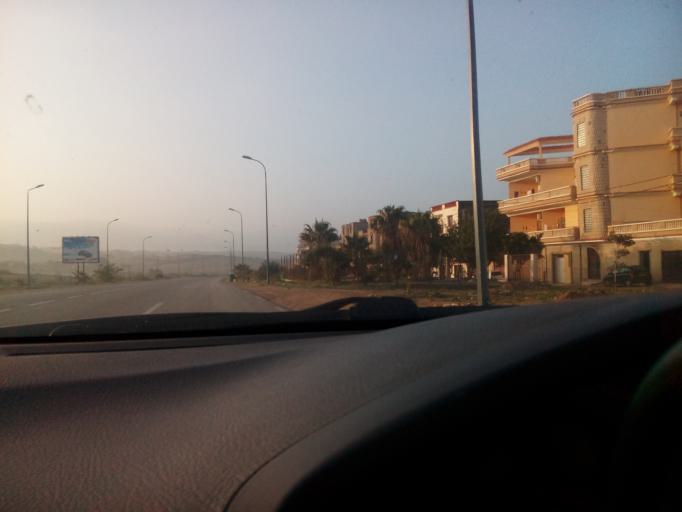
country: DZ
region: Oran
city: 'Ain el Turk
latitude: 35.7318
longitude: -0.8417
